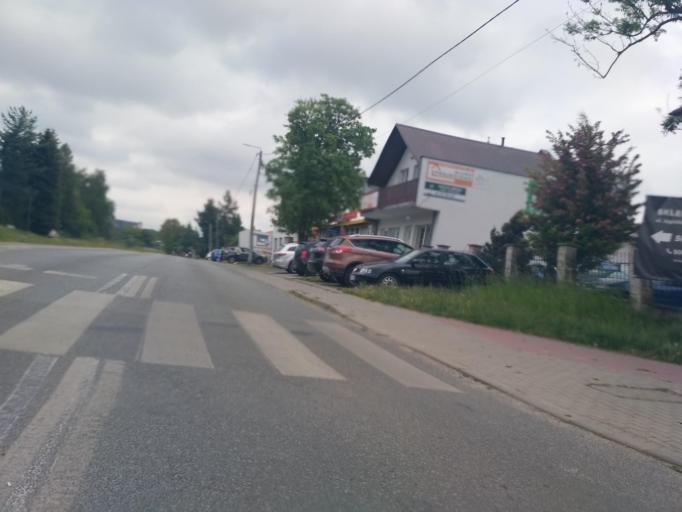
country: PL
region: Subcarpathian Voivodeship
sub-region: Krosno
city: Krosno
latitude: 49.6894
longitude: 21.7589
